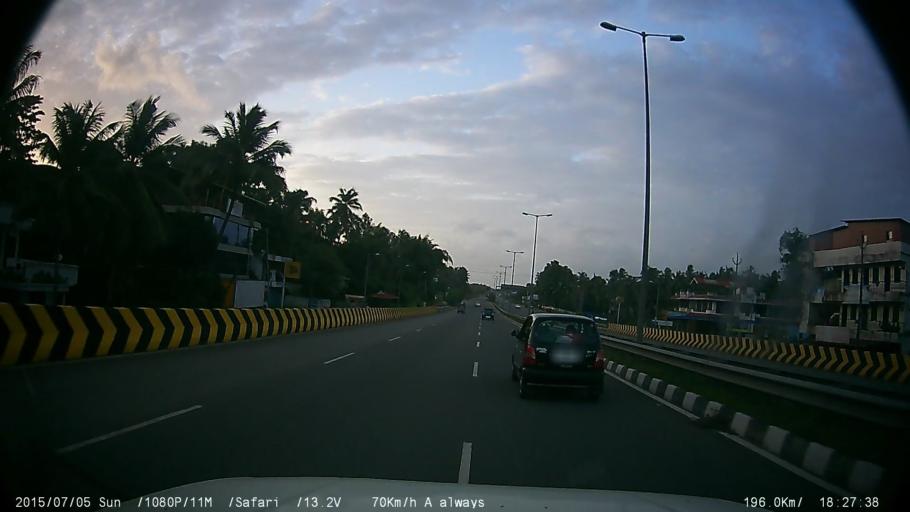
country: IN
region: Kerala
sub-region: Thrissur District
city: Trichur
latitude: 10.4519
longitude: 76.2585
